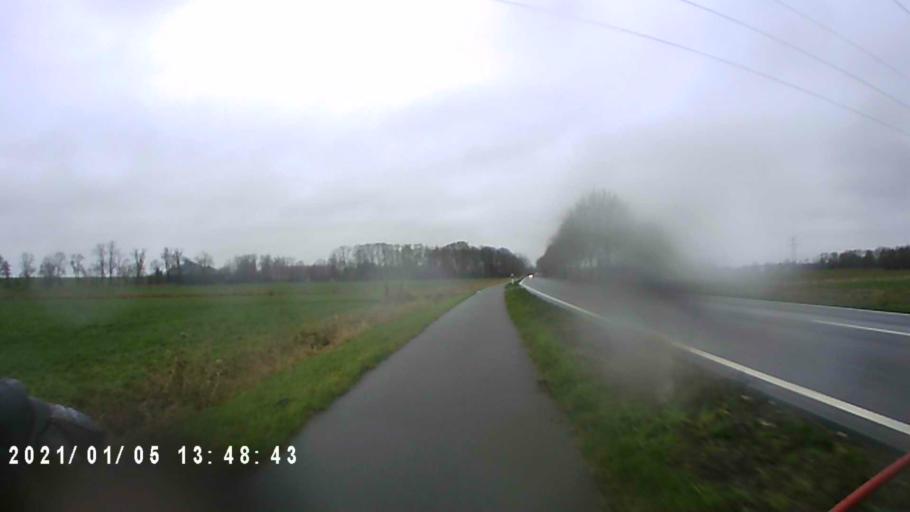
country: DE
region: Lower Saxony
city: Weener
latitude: 53.1789
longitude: 7.3736
